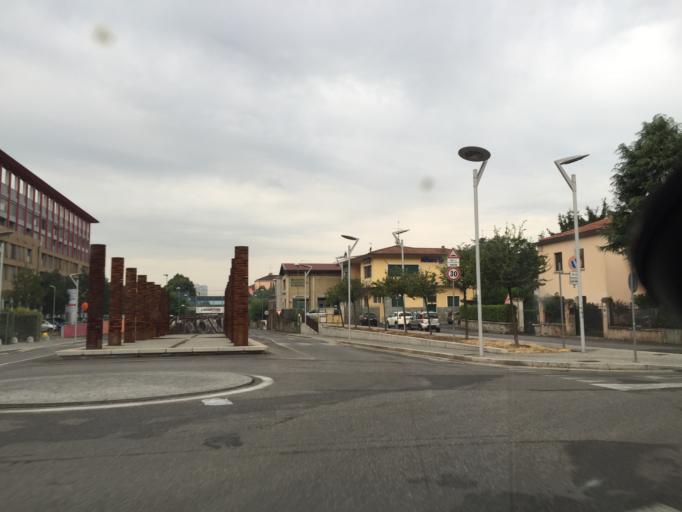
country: IT
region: Lombardy
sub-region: Provincia di Brescia
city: Brescia
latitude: 45.5357
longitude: 10.2019
